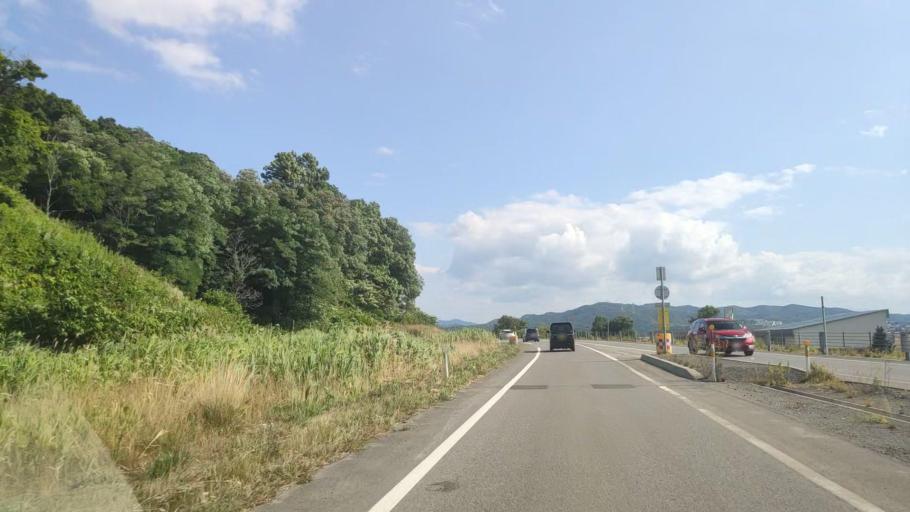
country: JP
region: Hokkaido
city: Rumoi
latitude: 43.9521
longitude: 141.6455
